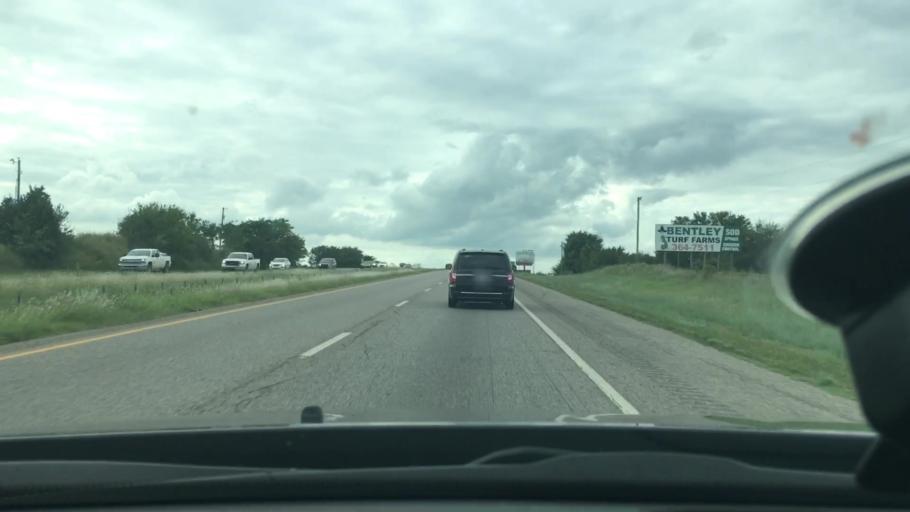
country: US
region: Oklahoma
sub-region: Cleveland County
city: Noble
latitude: 35.1045
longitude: -97.4316
